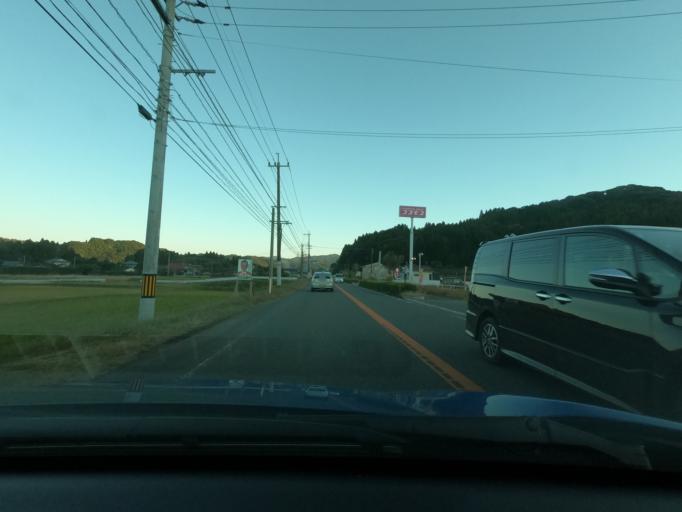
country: JP
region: Kagoshima
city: Satsumasendai
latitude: 31.7988
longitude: 130.4017
